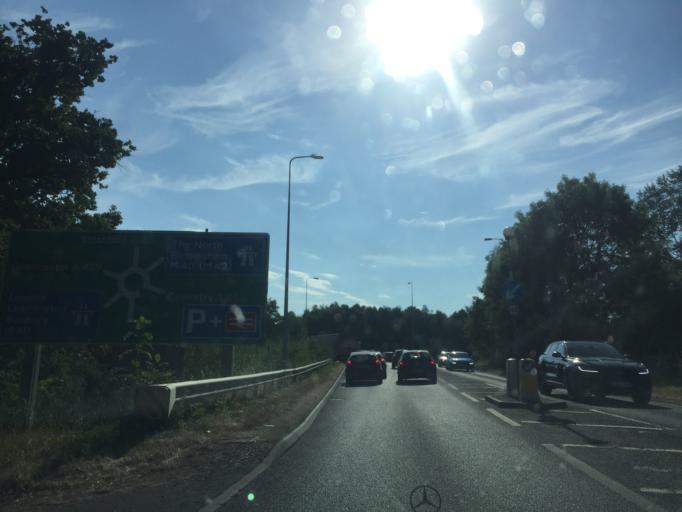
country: GB
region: England
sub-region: Warwickshire
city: Warwick
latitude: 52.2607
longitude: -1.6101
